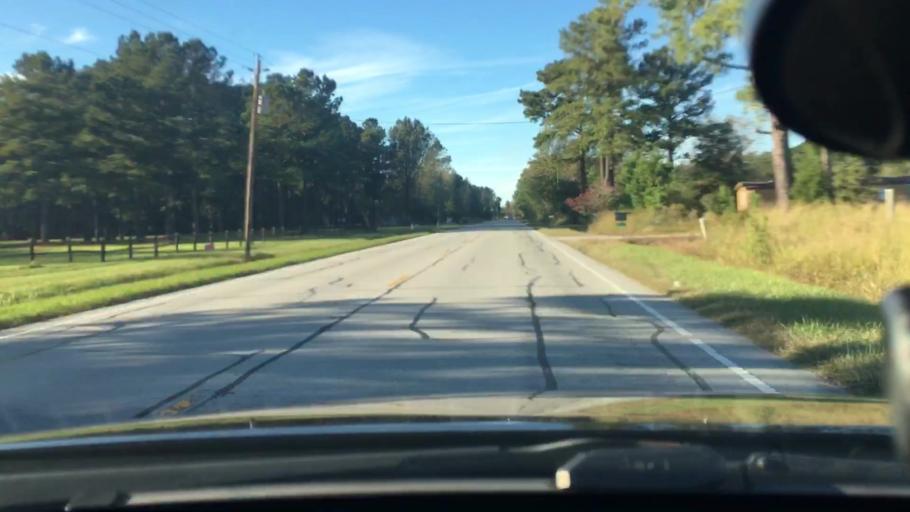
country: US
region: North Carolina
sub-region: Craven County
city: Vanceboro
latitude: 35.3214
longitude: -77.1655
